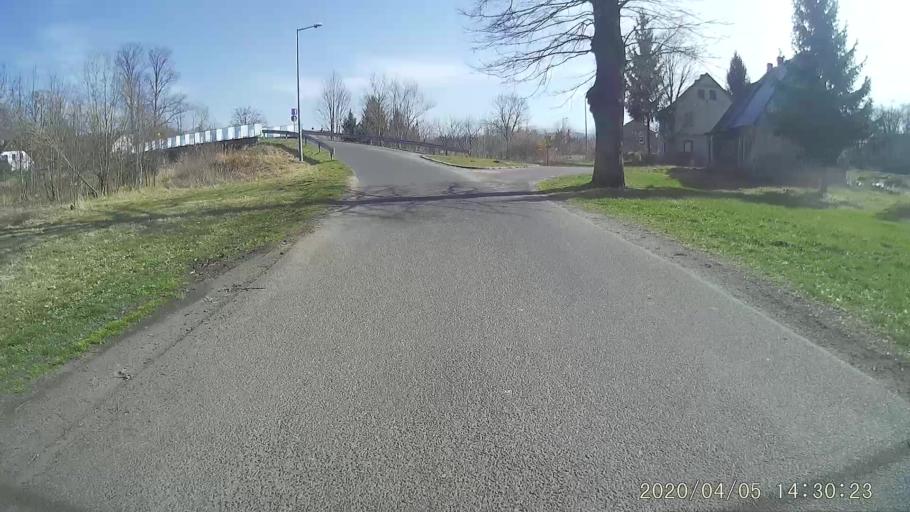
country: PL
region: Lower Silesian Voivodeship
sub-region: Powiat lubanski
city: Lesna
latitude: 51.0329
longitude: 15.2585
